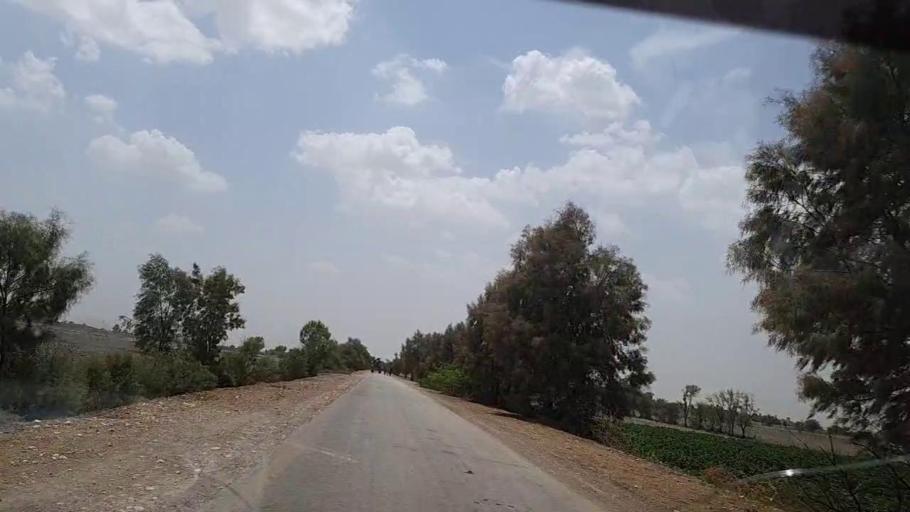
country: PK
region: Sindh
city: Bhan
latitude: 26.5408
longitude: 67.6694
